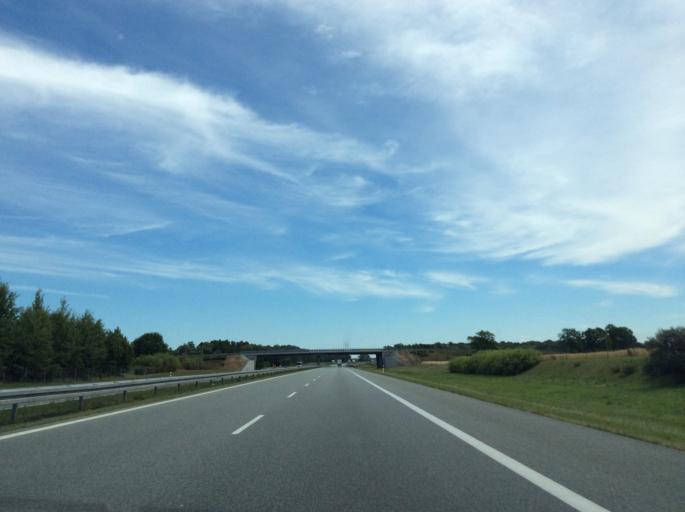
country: PL
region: Greater Poland Voivodeship
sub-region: Powiat poznanski
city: Buk
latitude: 52.3870
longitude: 16.4995
